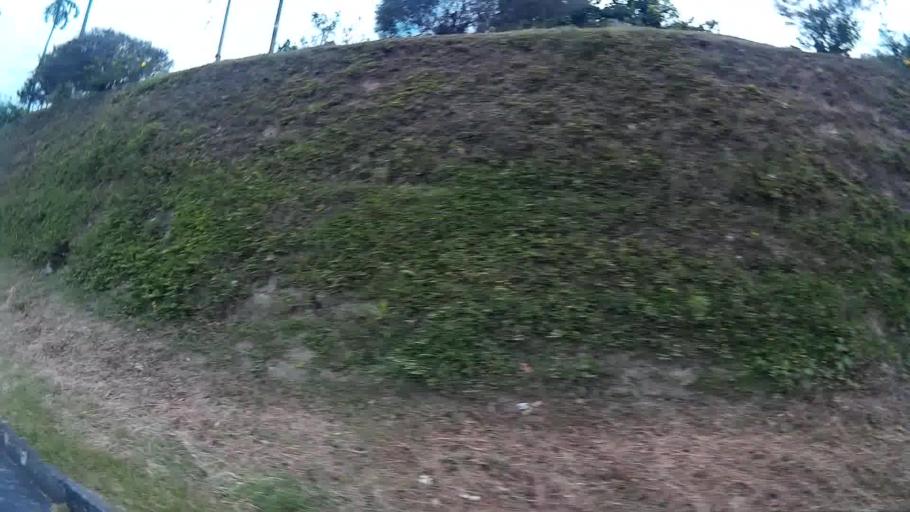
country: CO
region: Risaralda
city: Pereira
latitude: 4.7642
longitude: -75.6867
